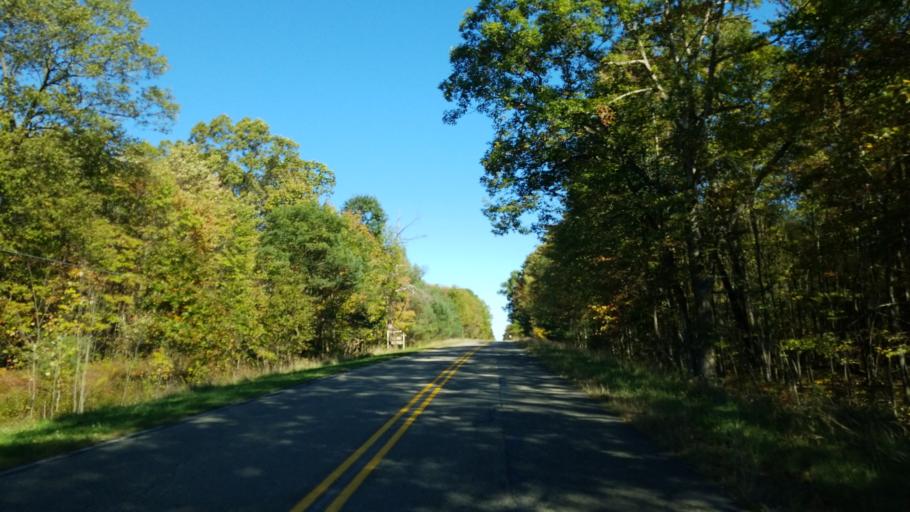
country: US
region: Pennsylvania
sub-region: Clearfield County
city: Shiloh
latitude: 41.2555
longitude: -78.3266
